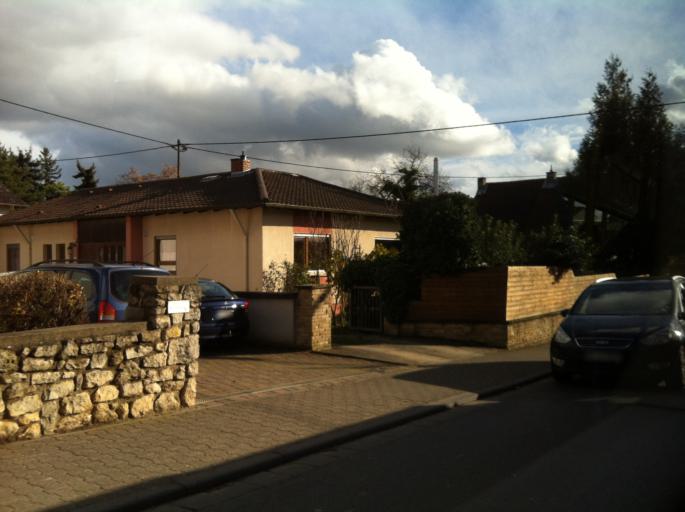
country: DE
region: Rheinland-Pfalz
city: Stadecken-Elsheim
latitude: 49.9195
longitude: 8.1259
